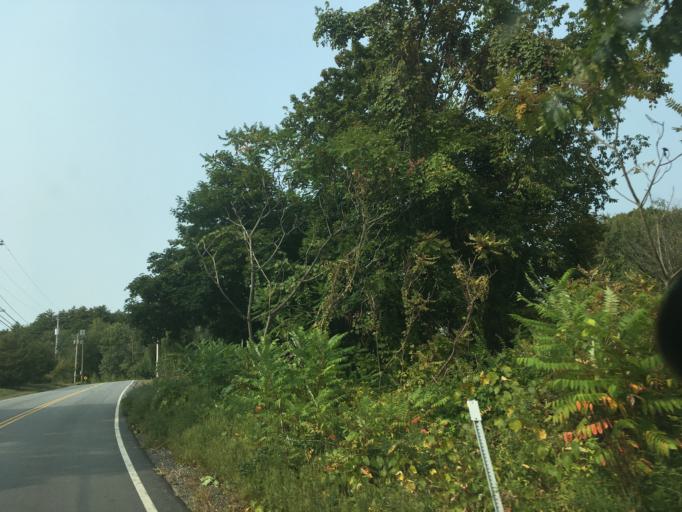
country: US
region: New Hampshire
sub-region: Rockingham County
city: Stratham Station
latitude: 43.0212
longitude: -70.8975
